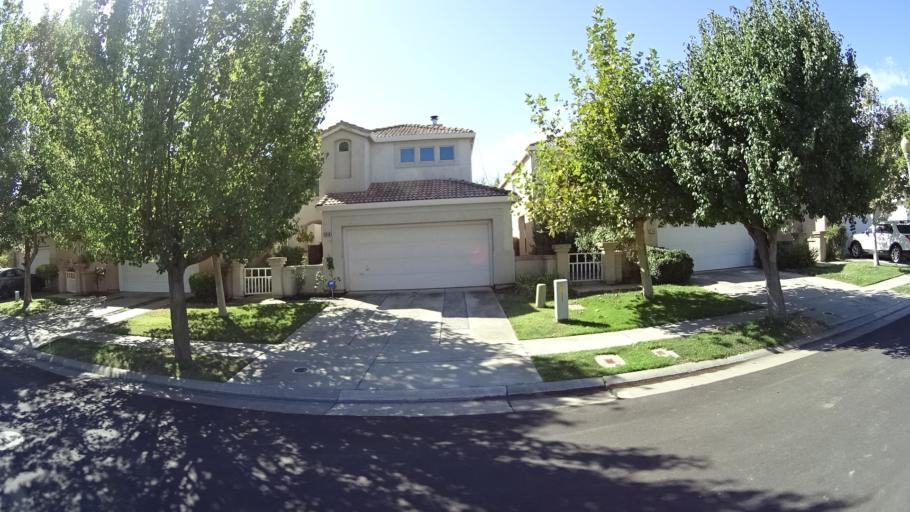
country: US
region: California
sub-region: Sacramento County
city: Laguna
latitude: 38.4231
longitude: -121.4714
